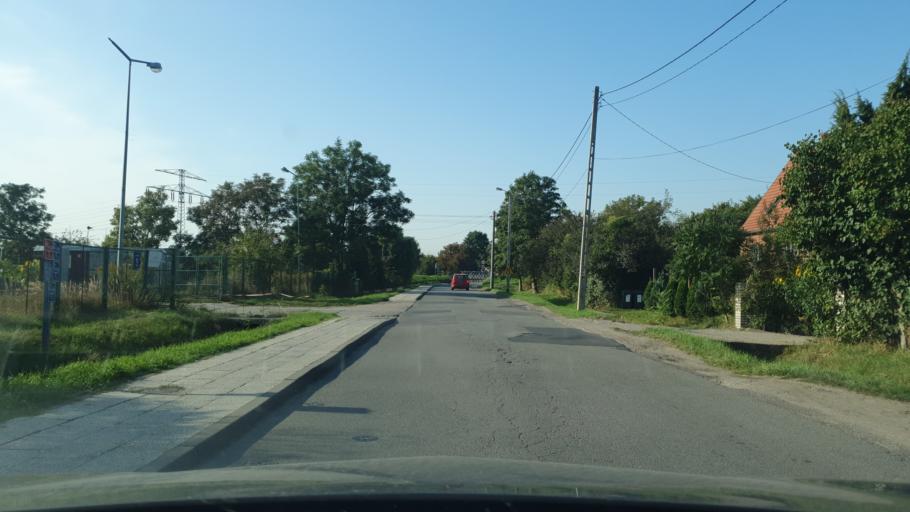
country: PL
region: Pomeranian Voivodeship
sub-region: Gdansk
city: Gdansk
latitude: 54.3467
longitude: 18.6812
